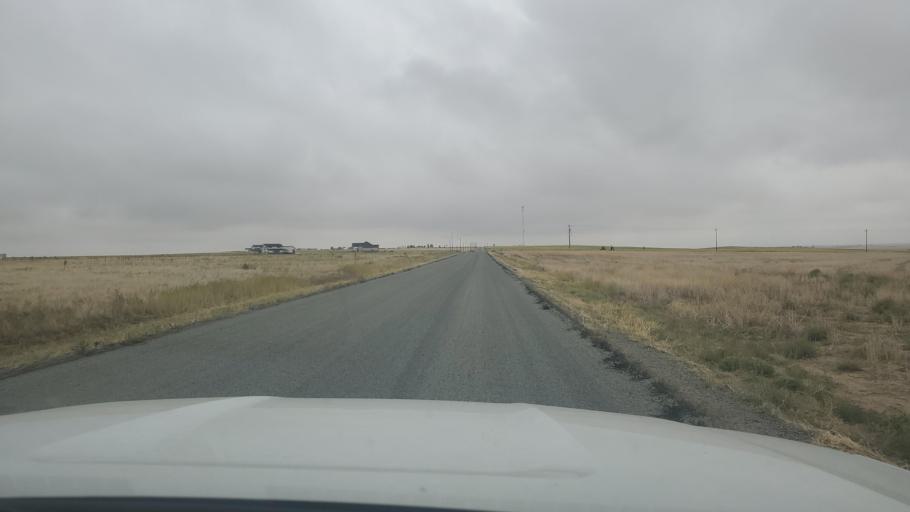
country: US
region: Colorado
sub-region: Weld County
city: Lochbuie
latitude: 39.9307
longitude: -104.6028
